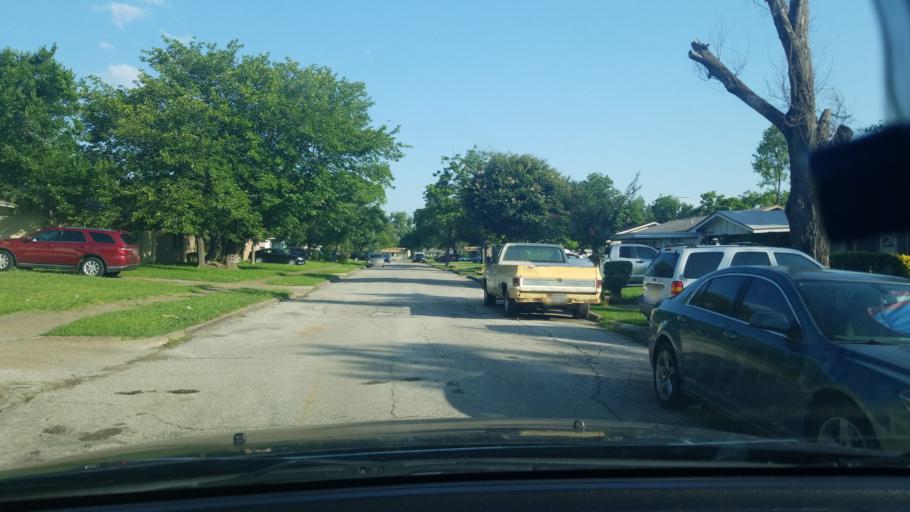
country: US
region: Texas
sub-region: Dallas County
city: Mesquite
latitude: 32.8107
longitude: -96.6364
